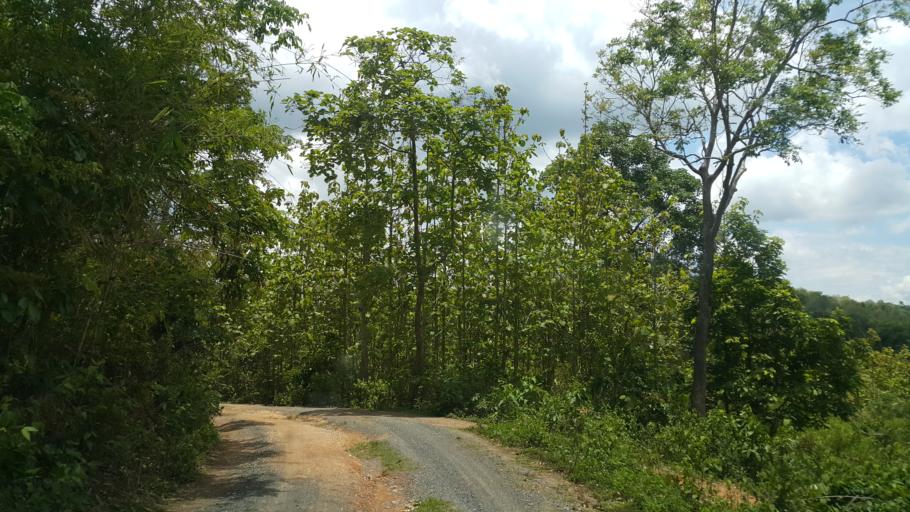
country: TH
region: Phayao
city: Phayao
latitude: 19.1734
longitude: 99.7816
